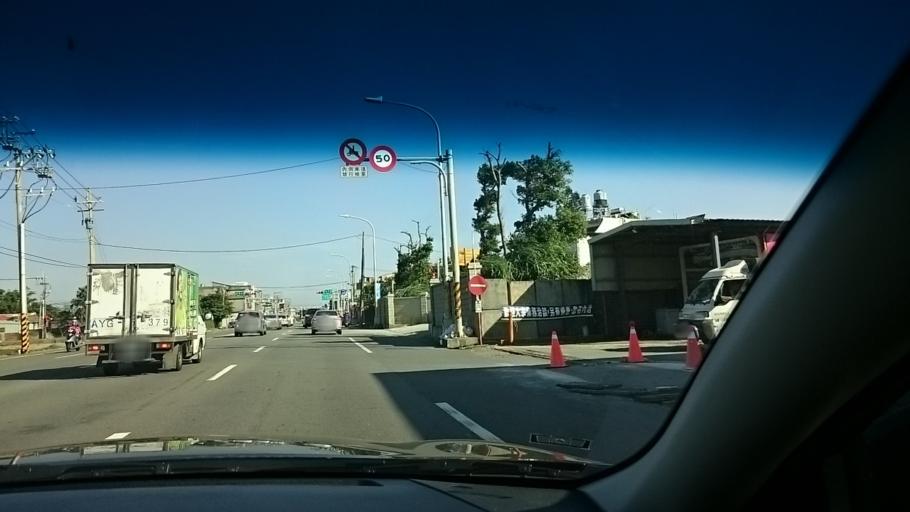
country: TW
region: Taiwan
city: Taoyuan City
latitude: 24.9723
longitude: 121.1290
